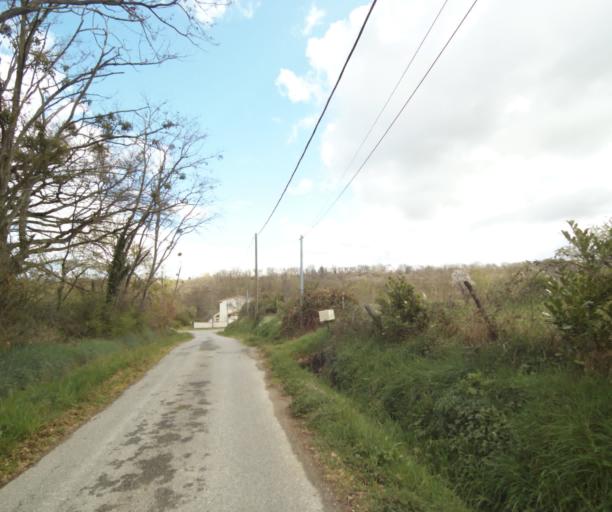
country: FR
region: Midi-Pyrenees
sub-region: Departement de l'Ariege
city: Saverdun
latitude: 43.2104
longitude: 1.5749
